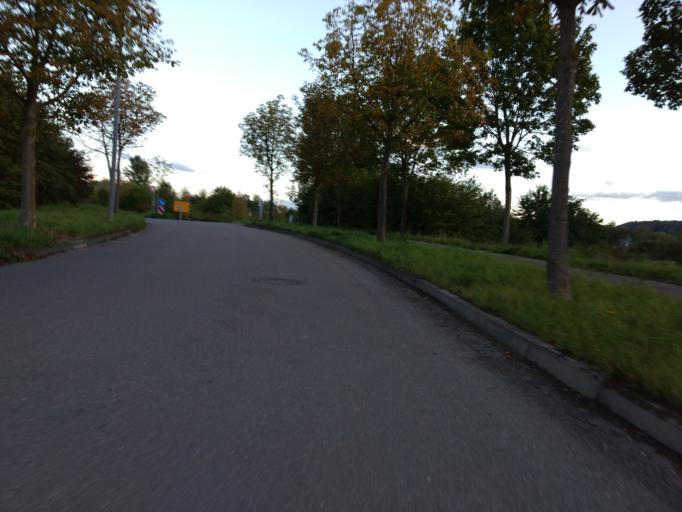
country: DE
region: Saarland
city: Rehlingen-Siersburg
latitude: 49.3713
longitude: 6.7057
